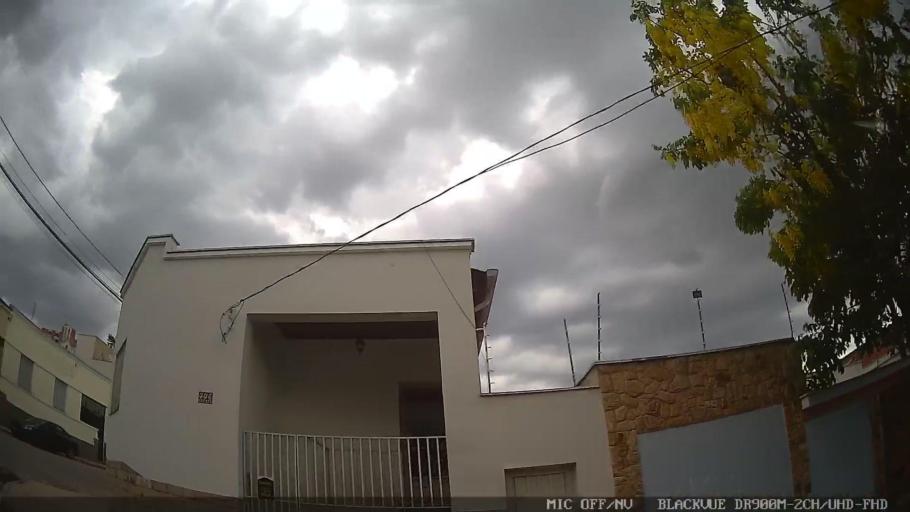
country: BR
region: Sao Paulo
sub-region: Amparo
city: Amparo
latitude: -22.7033
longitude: -46.7599
